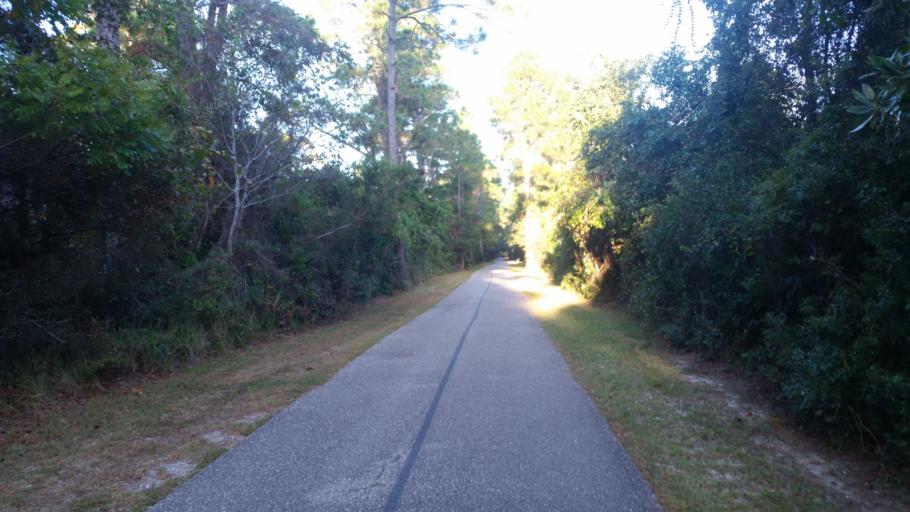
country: US
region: Alabama
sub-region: Baldwin County
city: Orange Beach
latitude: 30.2785
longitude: -87.5887
